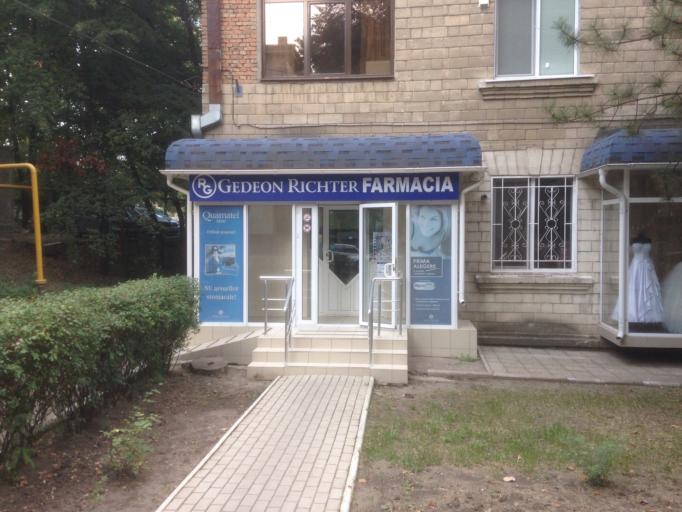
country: MD
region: Balti
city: Balti
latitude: 47.7623
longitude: 27.9270
